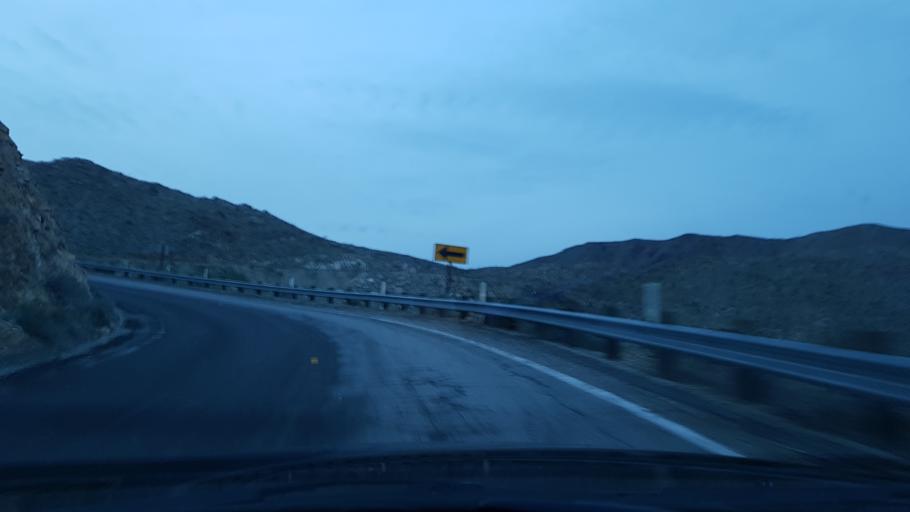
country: US
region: California
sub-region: San Diego County
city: Pine Valley
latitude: 32.9774
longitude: -116.4167
